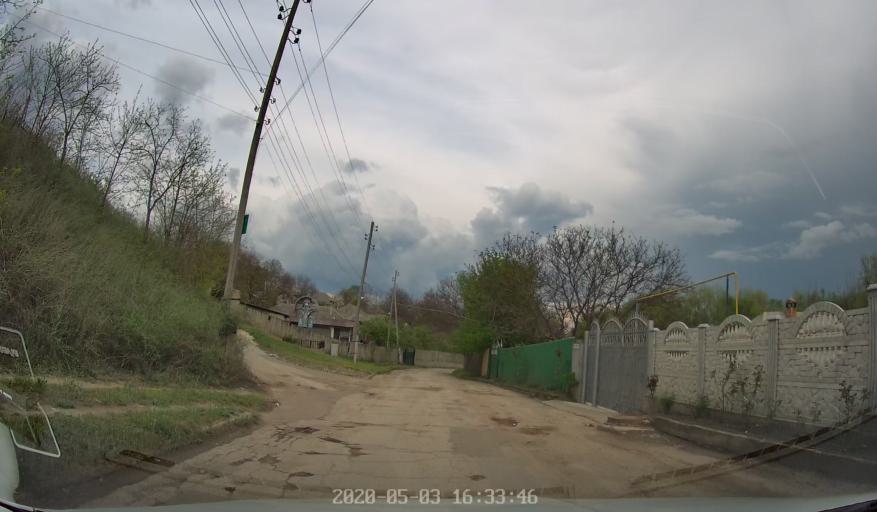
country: MD
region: Calarasi
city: Calarasi
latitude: 47.1913
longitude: 28.3429
